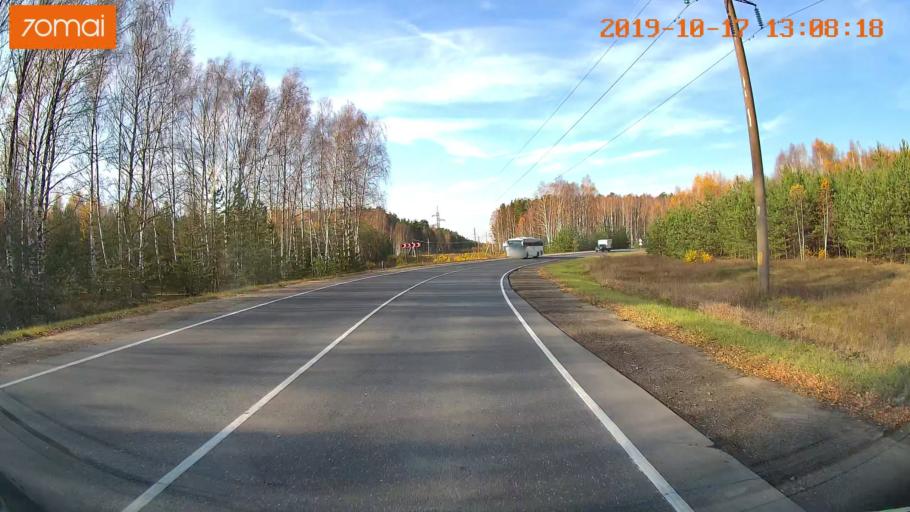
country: RU
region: Rjazan
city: Syntul
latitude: 54.9881
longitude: 41.2706
